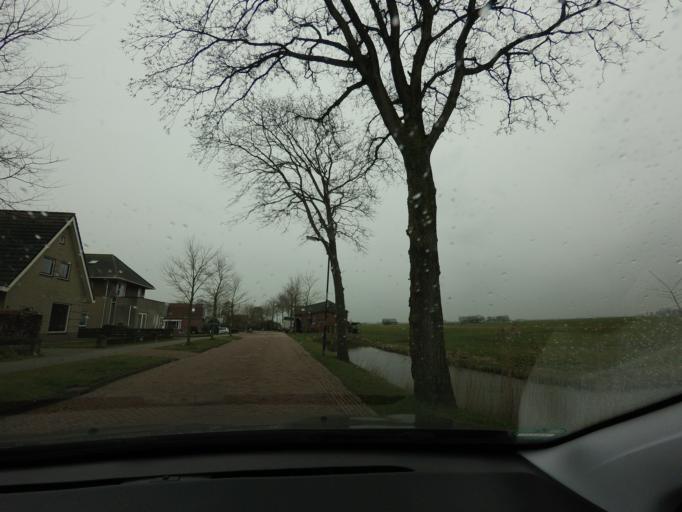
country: NL
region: Friesland
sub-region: Gemeente Franekeradeel
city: Tzum
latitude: 53.1609
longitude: 5.5606
